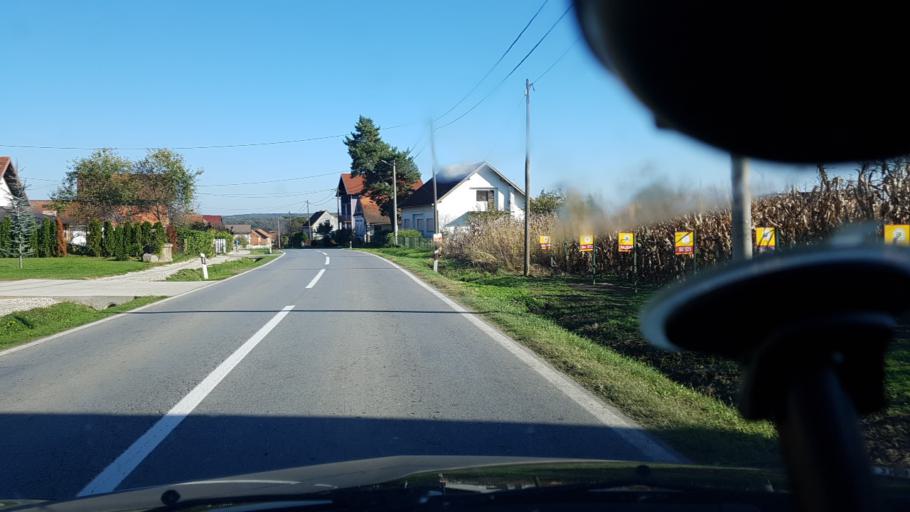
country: HR
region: Bjelovarsko-Bilogorska
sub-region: Grad Cazma
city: Cazma
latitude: 45.7826
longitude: 16.6629
